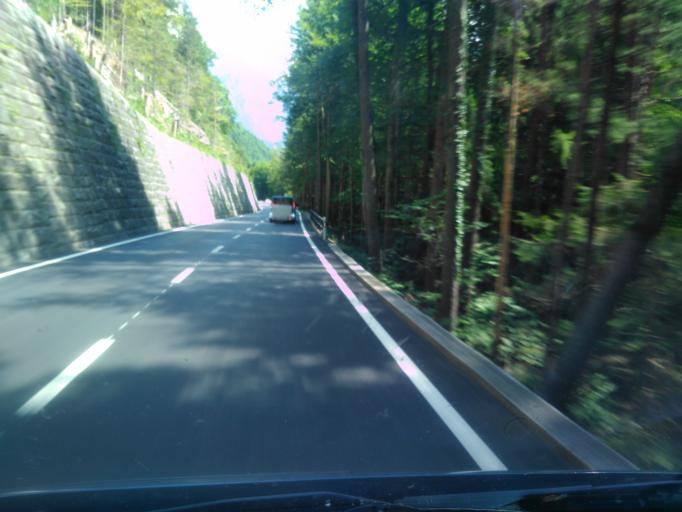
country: CH
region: Bern
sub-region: Interlaken-Oberhasli District
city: Meiringen
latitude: 46.7440
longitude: 8.1577
